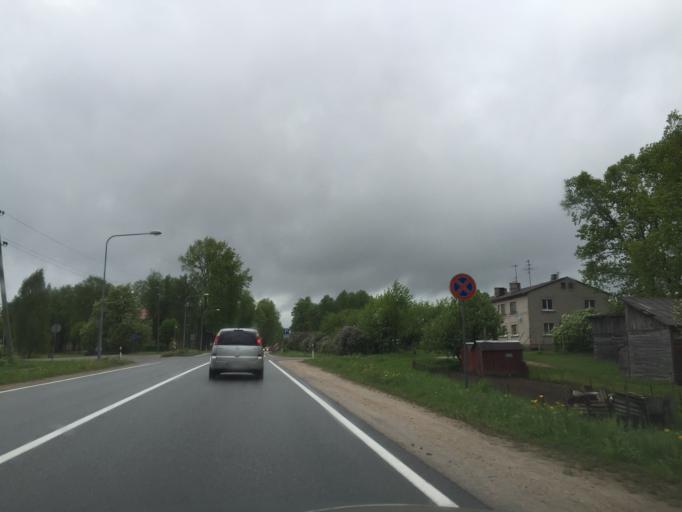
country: LV
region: Kegums
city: Kegums
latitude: 56.7395
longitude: 24.7270
